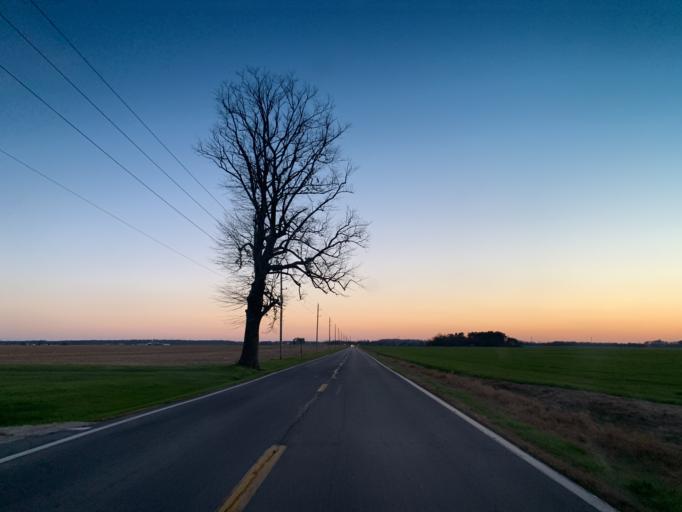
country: US
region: Delaware
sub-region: New Castle County
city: Middletown
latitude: 39.4161
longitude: -75.7451
